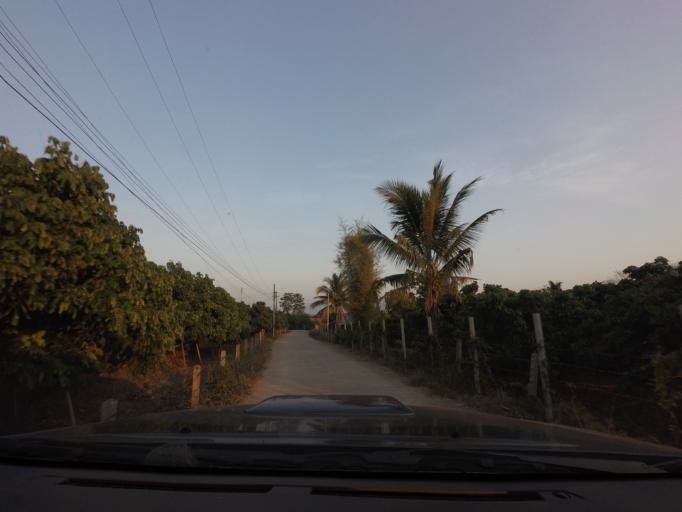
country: TH
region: Chiang Mai
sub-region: Amphoe Chiang Dao
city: Chiang Dao
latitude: 19.3680
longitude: 98.9573
